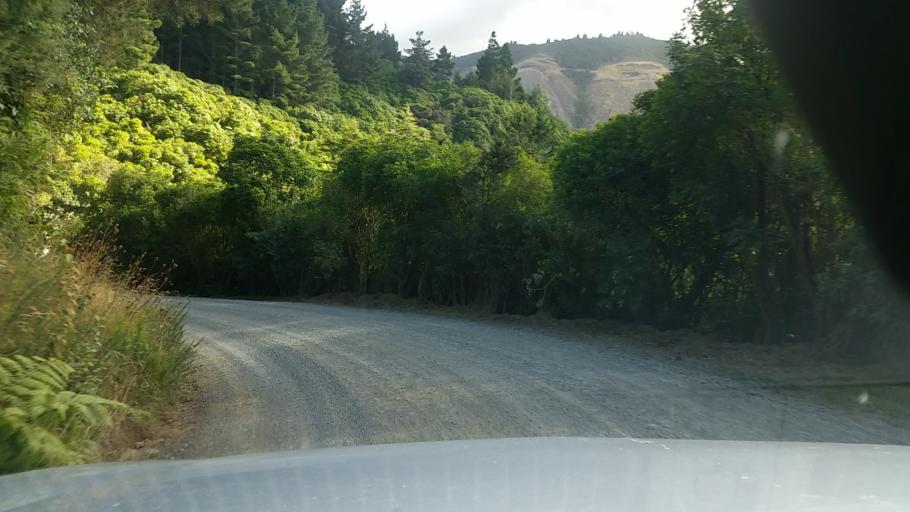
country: NZ
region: Marlborough
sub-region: Marlborough District
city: Picton
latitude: -41.2855
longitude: 174.1321
